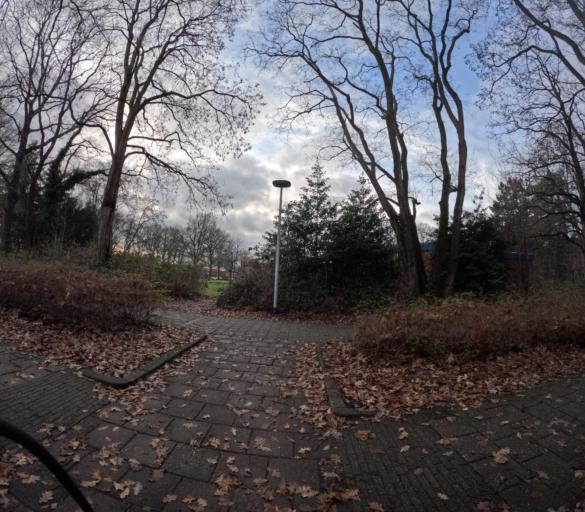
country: NL
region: Drenthe
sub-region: Gemeente Emmen
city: Emmen
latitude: 52.7834
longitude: 6.9241
